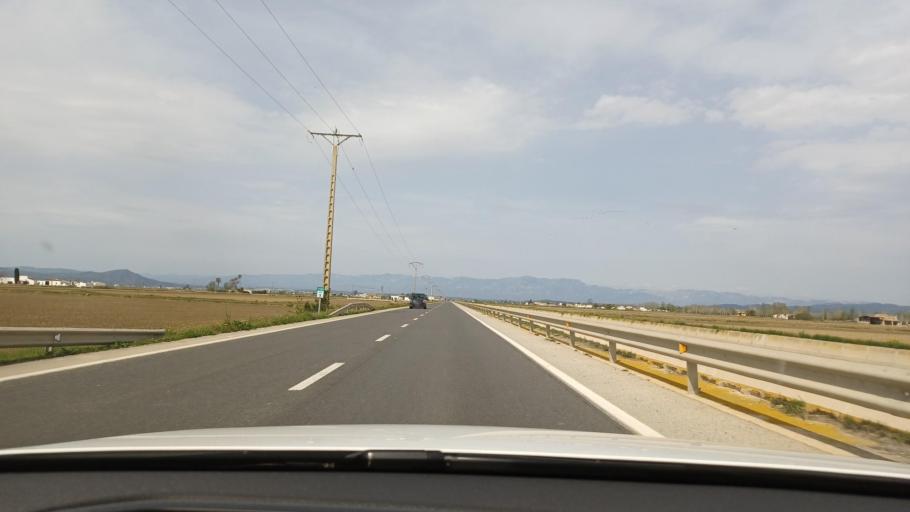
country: ES
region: Catalonia
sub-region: Provincia de Tarragona
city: Deltebre
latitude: 40.7075
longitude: 0.6967
